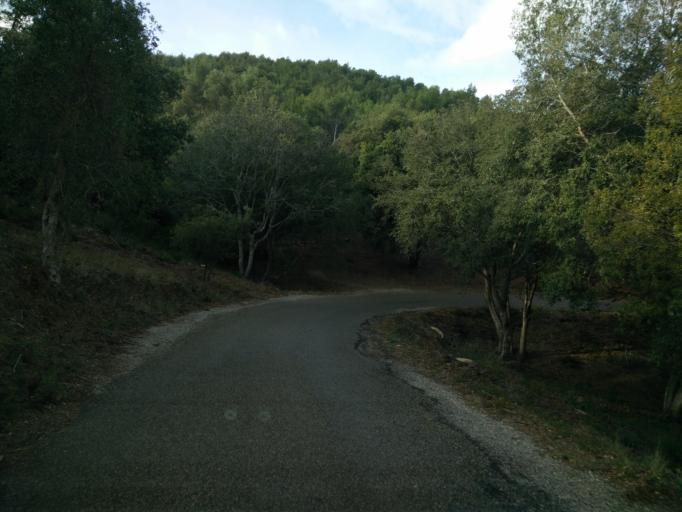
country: FR
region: Provence-Alpes-Cote d'Azur
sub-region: Departement du Var
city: Six-Fours-les-Plages
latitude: 43.0575
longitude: 5.8357
